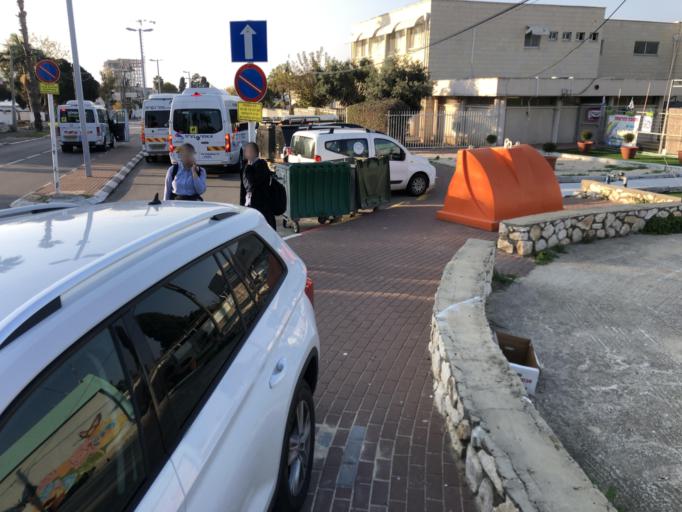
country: IL
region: Northern District
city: `Akko
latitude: 32.9262
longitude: 35.0899
